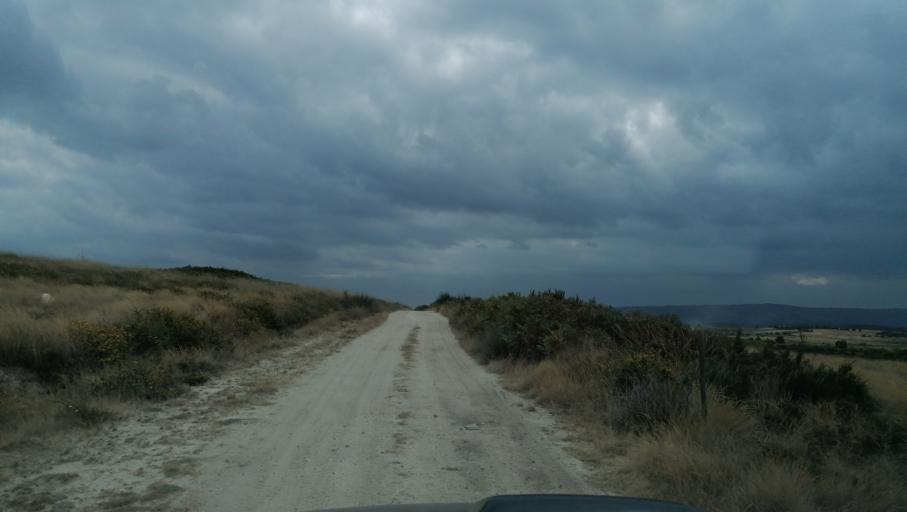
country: PT
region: Vila Real
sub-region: Vila Pouca de Aguiar
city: Vila Pouca de Aguiar
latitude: 41.5365
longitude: -7.7010
